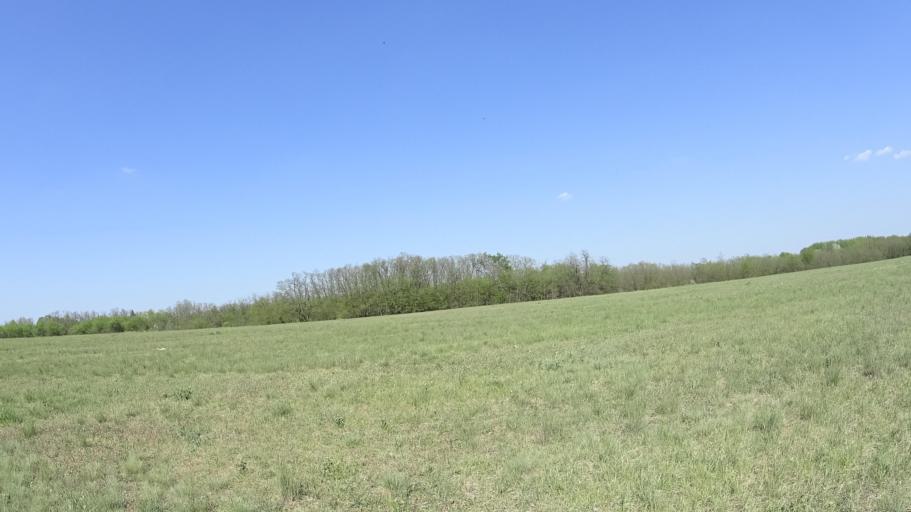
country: HU
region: Pest
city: Vecses
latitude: 47.4416
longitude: 19.2716
